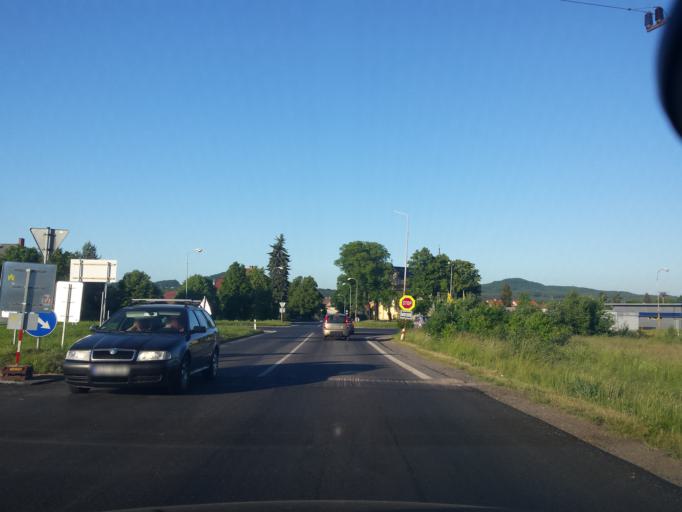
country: CZ
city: Duba
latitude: 50.6077
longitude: 14.5807
